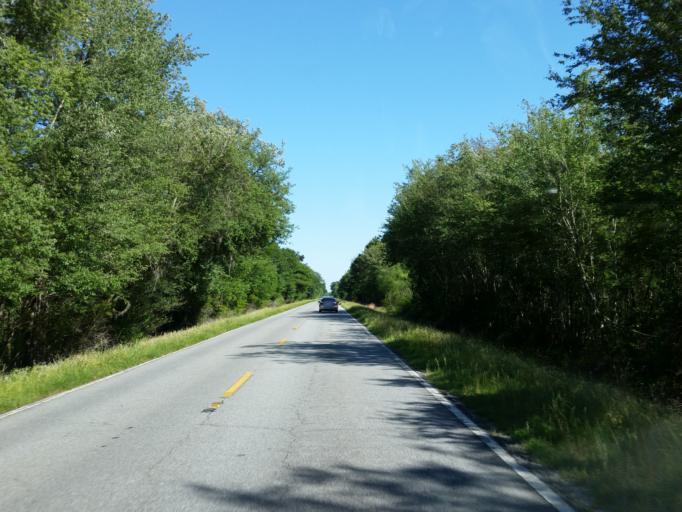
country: US
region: Georgia
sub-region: Echols County
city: Statenville
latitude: 30.6511
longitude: -83.1458
